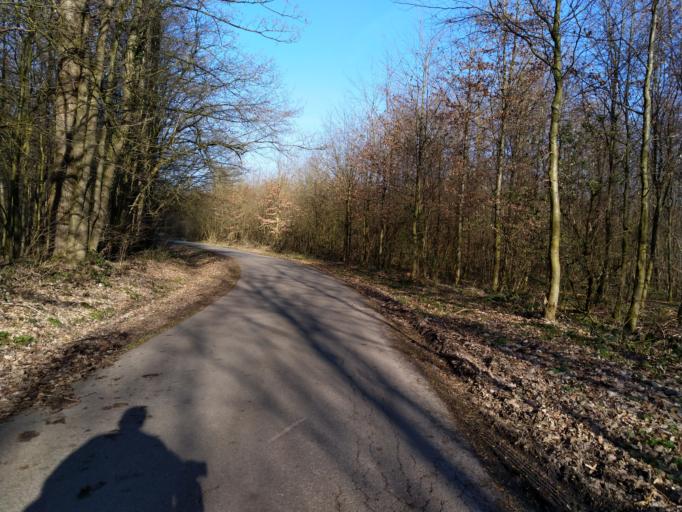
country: BE
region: Wallonia
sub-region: Province du Hainaut
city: Mons
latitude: 50.5202
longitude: 3.9849
